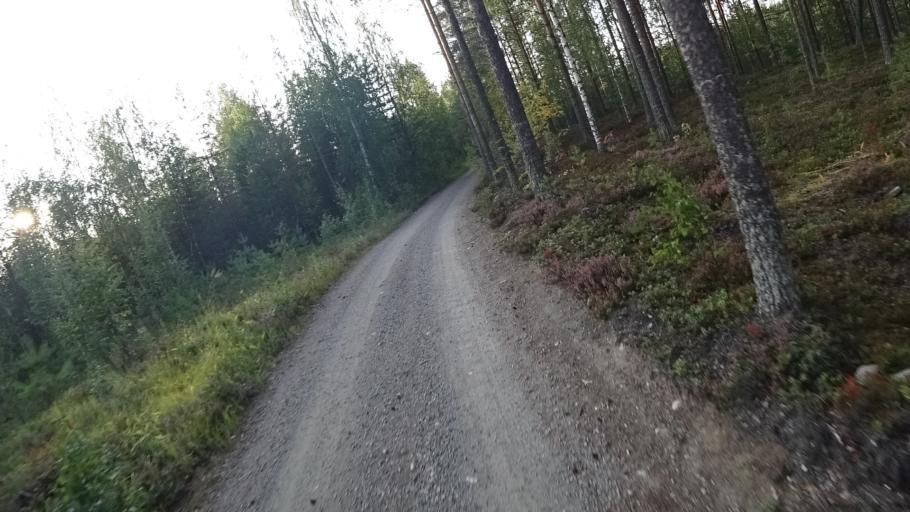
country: FI
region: North Karelia
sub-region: Joensuu
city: Ilomantsi
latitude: 62.6367
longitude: 31.0799
